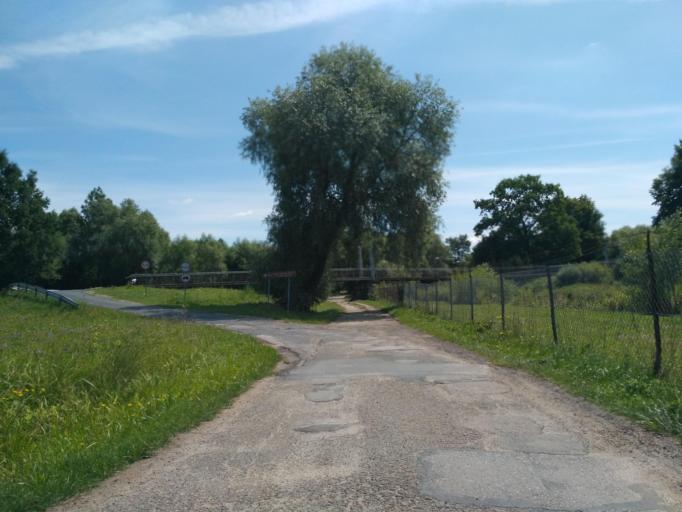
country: PL
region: Subcarpathian Voivodeship
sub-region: Powiat krosnienski
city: Kroscienko Wyzne
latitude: 49.6815
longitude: 21.8586
